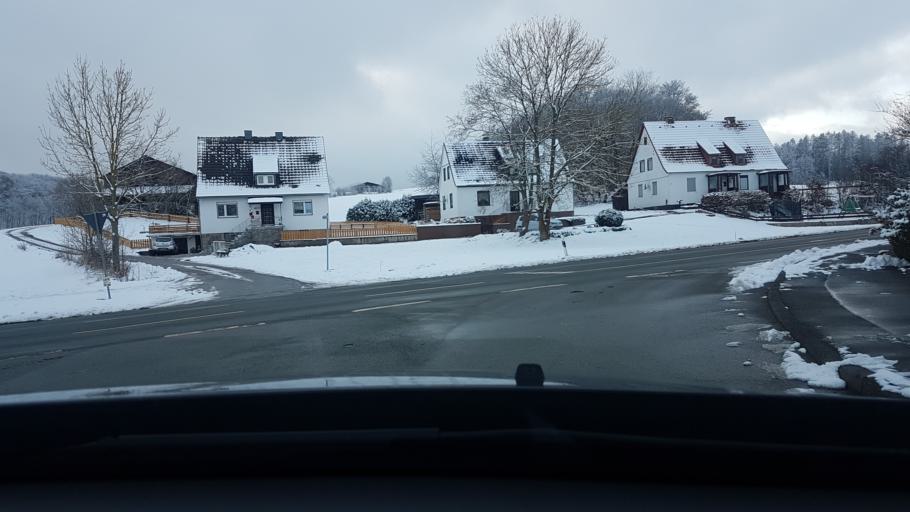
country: DE
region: North Rhine-Westphalia
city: Marsberg
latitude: 51.3567
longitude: 8.7659
